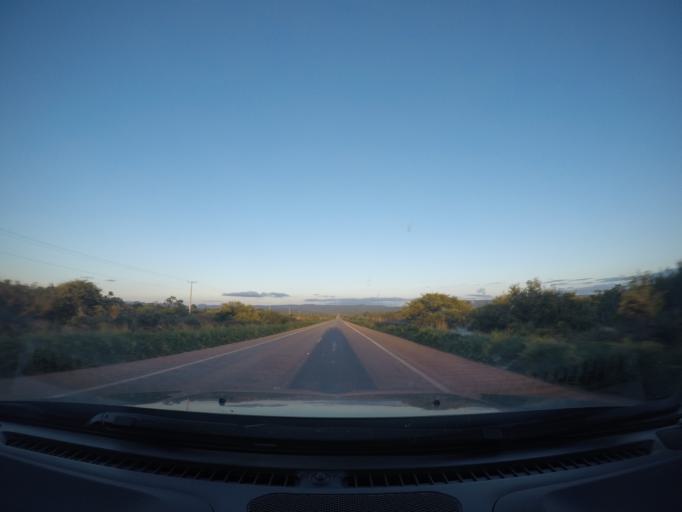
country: BR
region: Bahia
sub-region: Seabra
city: Seabra
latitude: -12.4080
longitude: -41.9634
